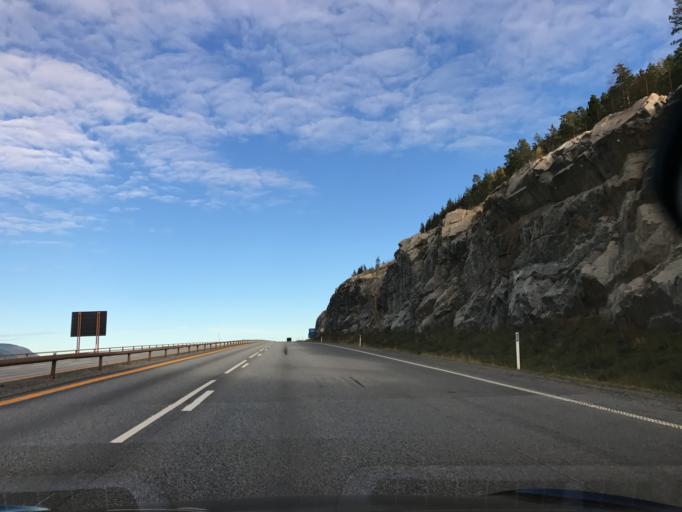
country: NO
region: Akershus
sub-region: Eidsvoll
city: Eidsvoll
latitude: 60.5170
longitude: 11.2435
